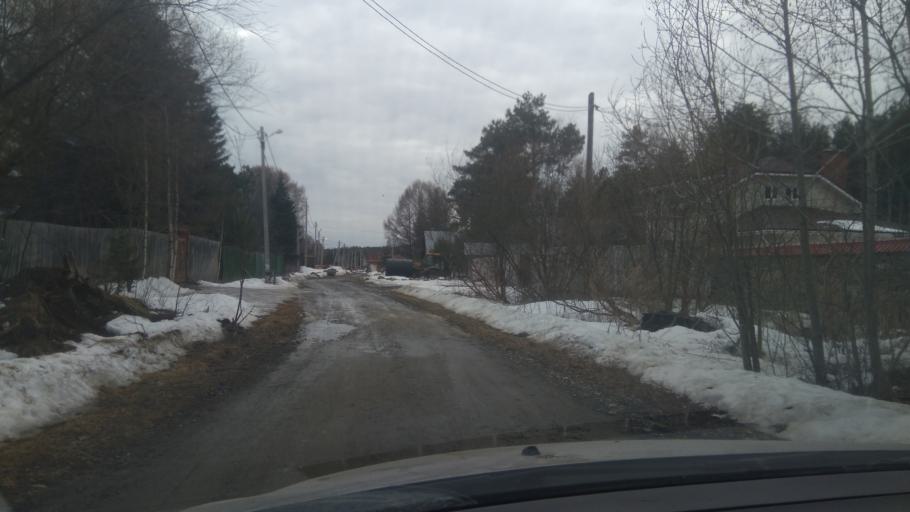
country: RU
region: Sverdlovsk
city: Severka
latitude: 56.8540
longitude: 60.3846
